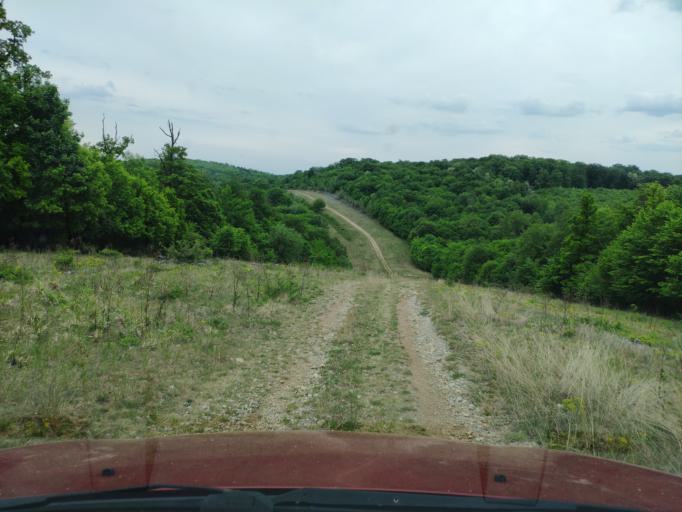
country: SK
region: Kosicky
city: Roznava
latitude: 48.5452
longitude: 20.5865
